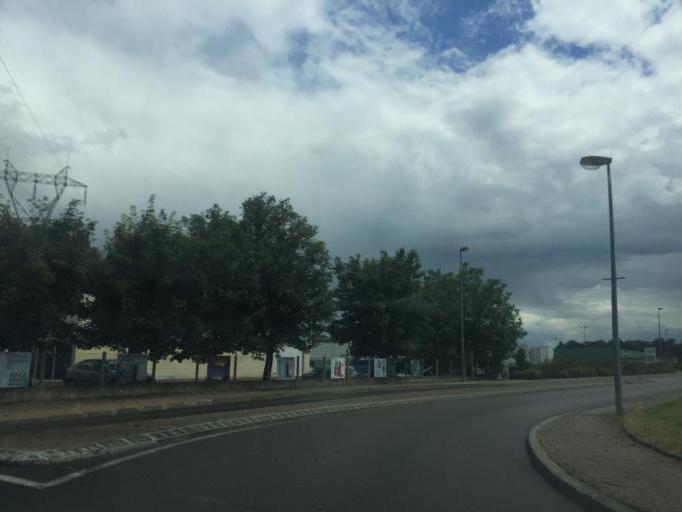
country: FR
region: Rhone-Alpes
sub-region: Departement de l'Isere
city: Janneyrias
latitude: 45.7925
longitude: 5.1290
